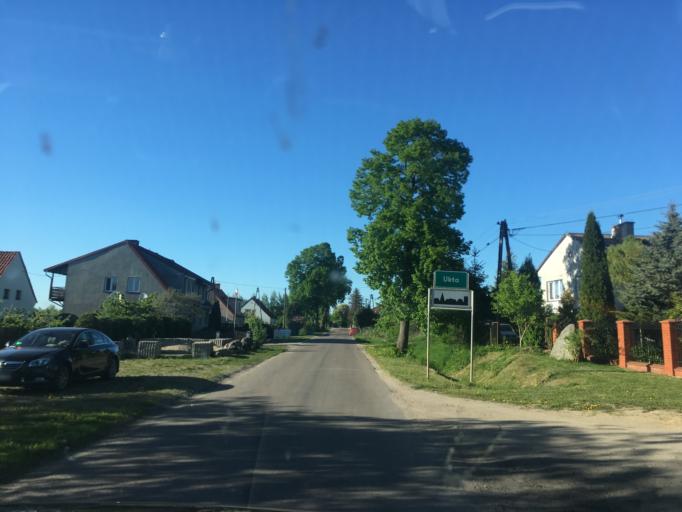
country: PL
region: Warmian-Masurian Voivodeship
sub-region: Powiat piski
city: Ruciane-Nida
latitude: 53.6833
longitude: 21.4992
